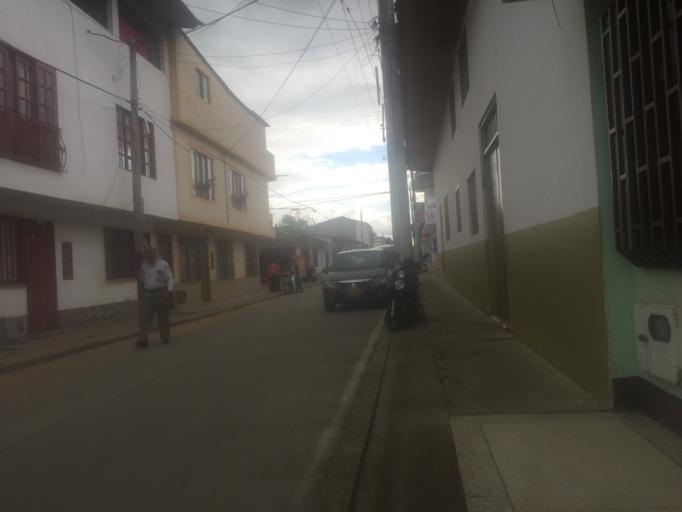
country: CO
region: Valle del Cauca
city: Calimita
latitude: 3.9329
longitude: -76.4848
